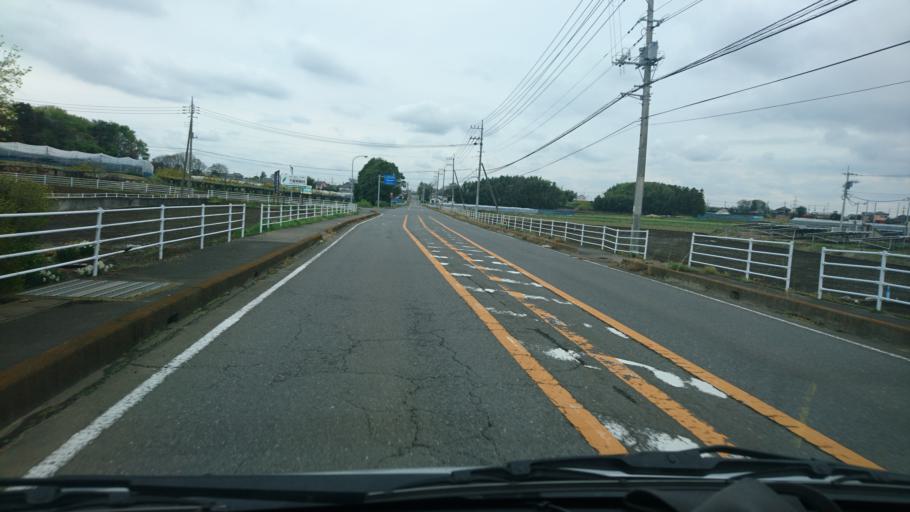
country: JP
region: Ibaraki
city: Yuki
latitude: 36.2622
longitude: 139.9287
